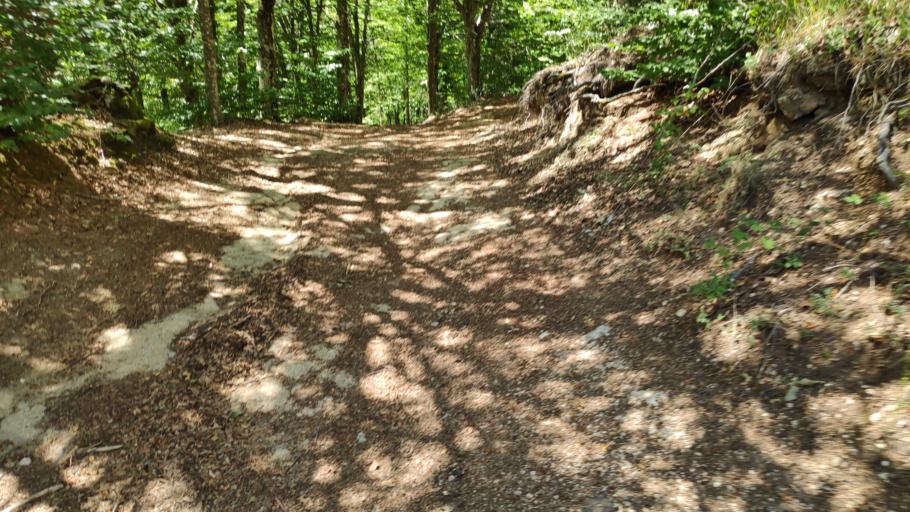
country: IT
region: Calabria
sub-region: Provincia di Vibo-Valentia
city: Mongiana
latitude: 38.5326
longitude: 16.3733
